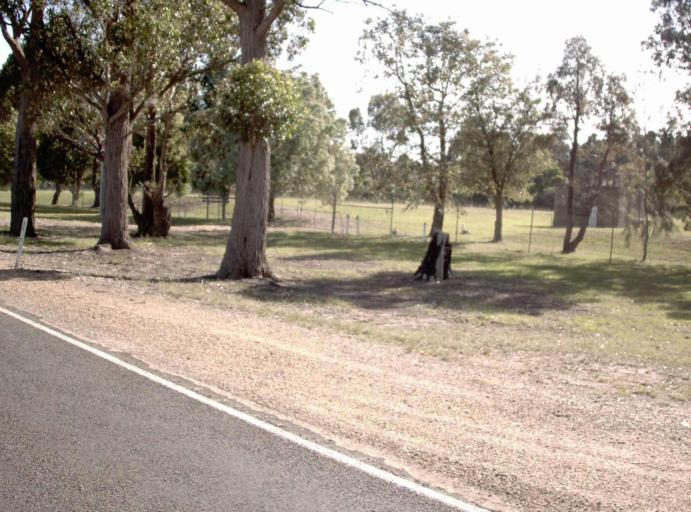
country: AU
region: Victoria
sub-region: East Gippsland
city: Lakes Entrance
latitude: -37.6925
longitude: 148.4687
